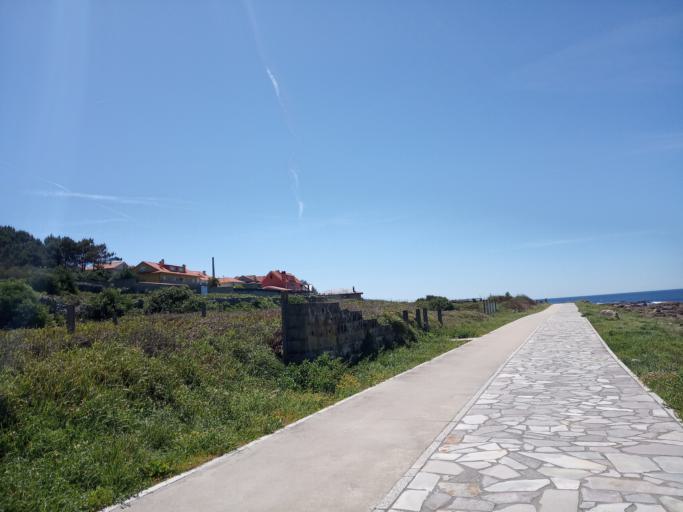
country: ES
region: Galicia
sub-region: Provincia de Pontevedra
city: A Guarda
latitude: 41.8869
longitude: -8.8809
